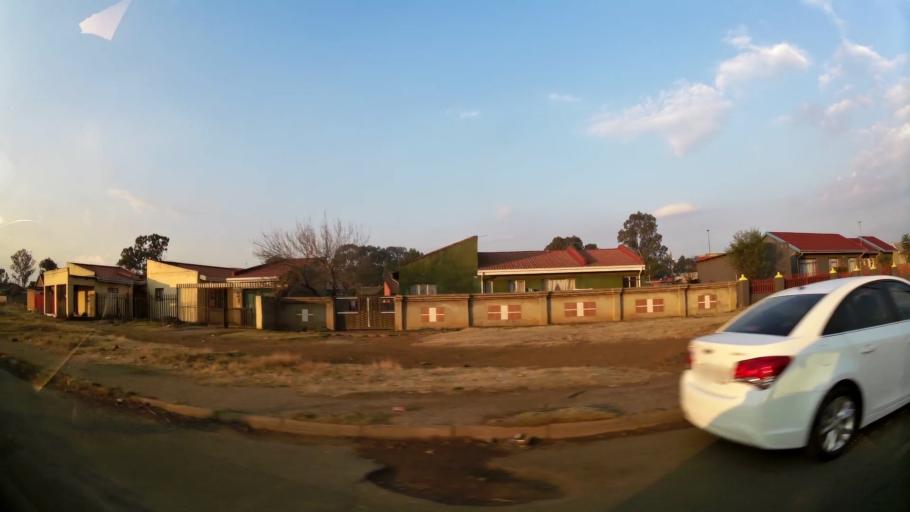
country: ZA
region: Gauteng
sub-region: City of Johannesburg Metropolitan Municipality
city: Orange Farm
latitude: -26.5393
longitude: 27.8843
